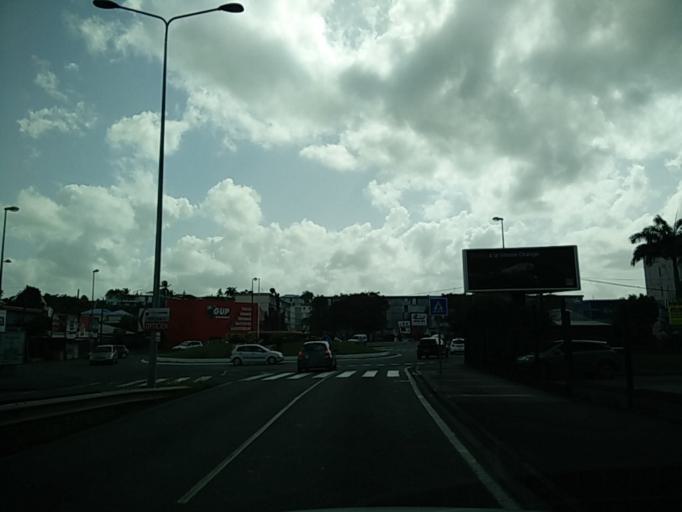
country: GP
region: Guadeloupe
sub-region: Guadeloupe
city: Pointe-a-Pitre
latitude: 16.2514
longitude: -61.5212
